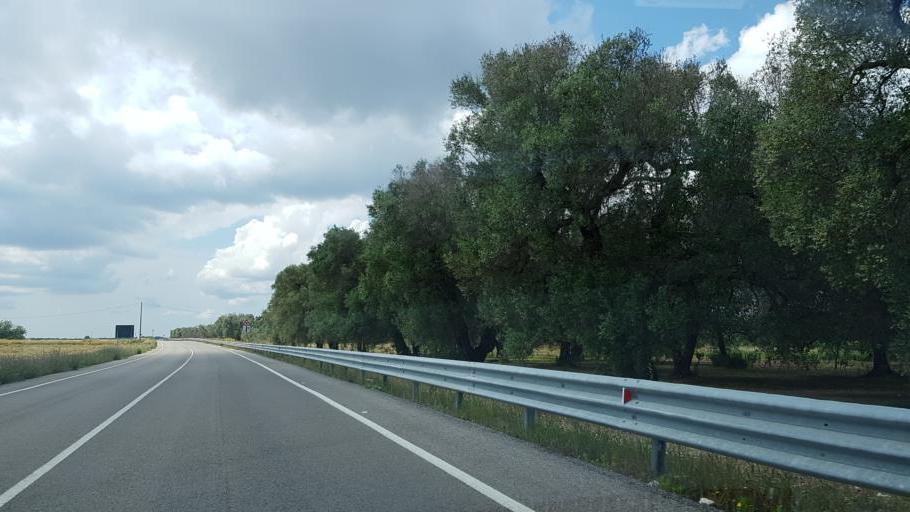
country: IT
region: Apulia
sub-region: Provincia di Brindisi
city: Mesagne
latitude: 40.5086
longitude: 17.8272
